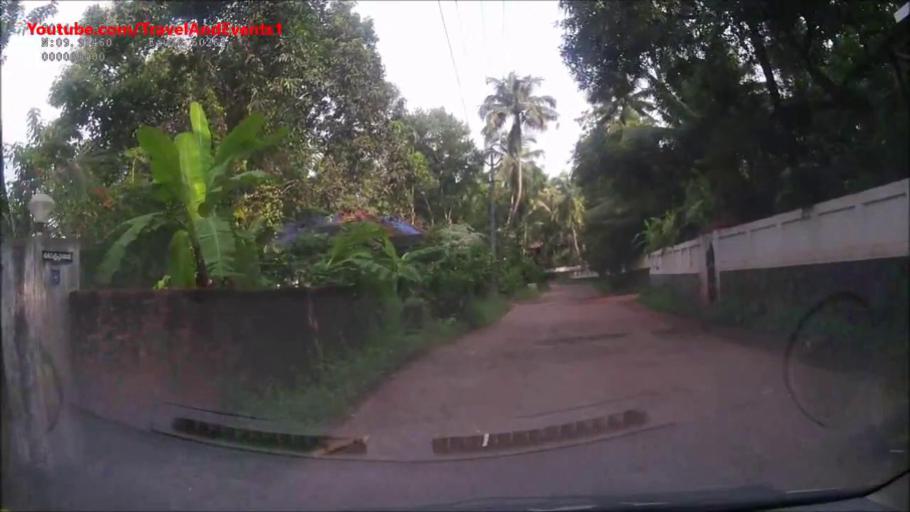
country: IN
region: Kerala
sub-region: Ernakulam
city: Muvattupula
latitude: 9.9687
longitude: 76.6100
